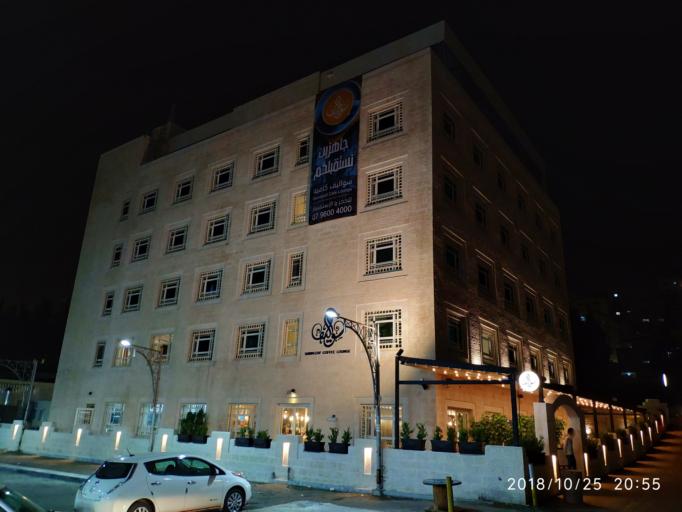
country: JO
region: Amman
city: Al Jubayhah
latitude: 32.0148
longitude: 35.8676
